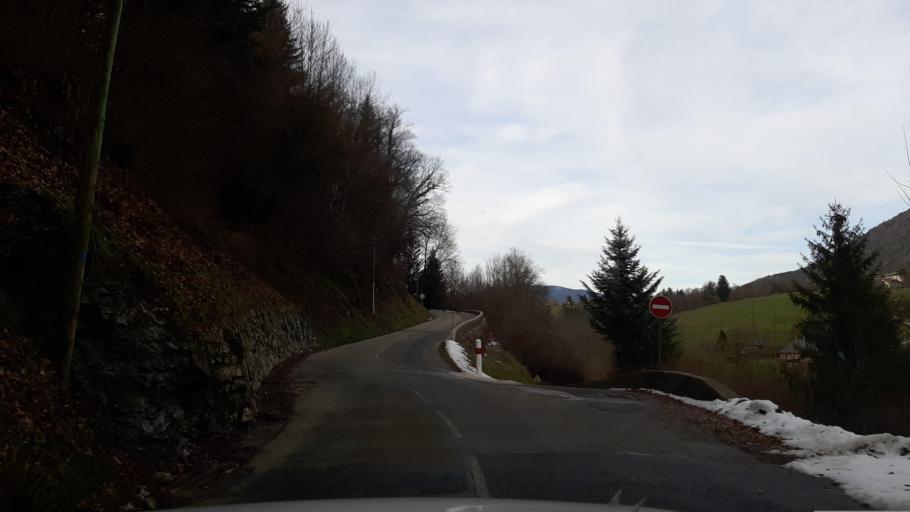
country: FR
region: Rhone-Alpes
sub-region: Departement de la Haute-Savoie
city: Doussard
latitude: 45.6775
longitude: 6.1334
